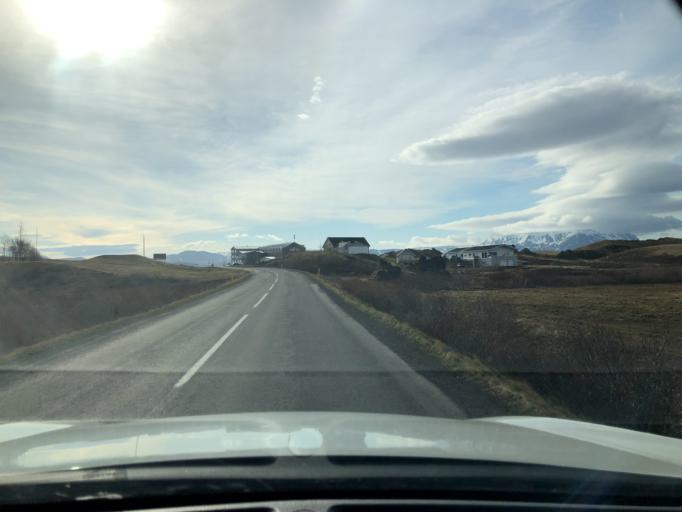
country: IS
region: Northeast
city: Laugar
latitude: 65.5686
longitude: -17.0434
